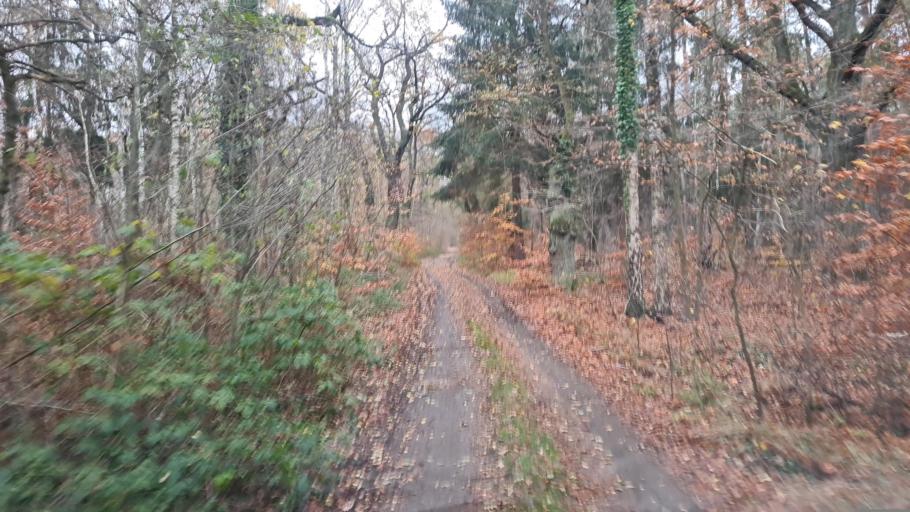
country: DE
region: Brandenburg
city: Crinitz
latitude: 51.7508
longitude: 13.7904
